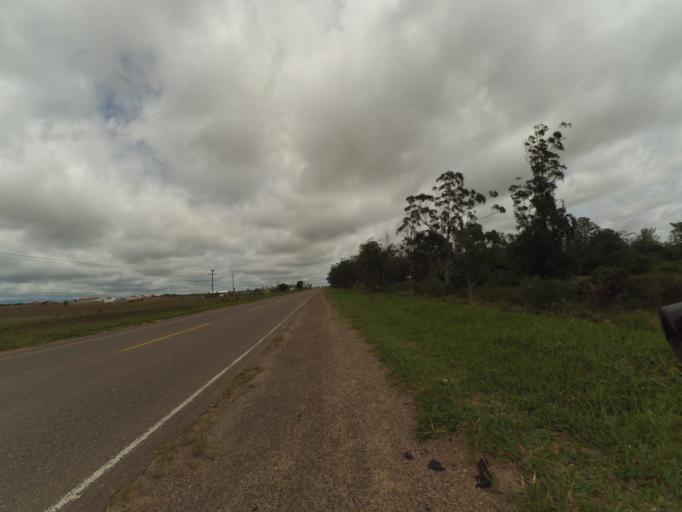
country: BO
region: Santa Cruz
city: Santa Rita
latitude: -17.9047
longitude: -63.2533
